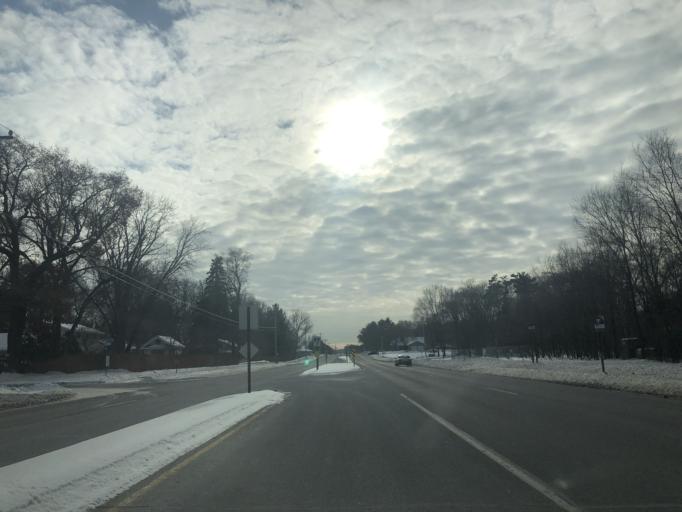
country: US
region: Minnesota
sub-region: Anoka County
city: Lexington
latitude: 45.1483
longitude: -93.1635
